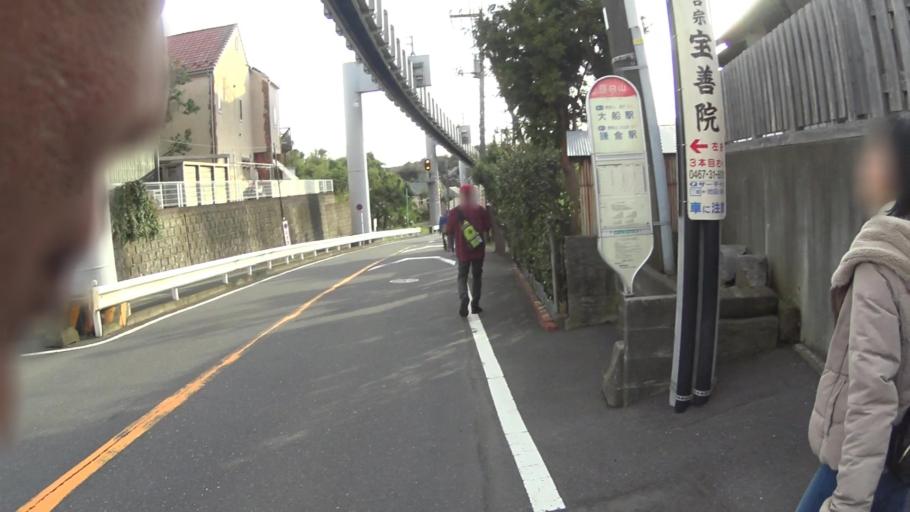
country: JP
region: Kanagawa
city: Fujisawa
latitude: 35.3152
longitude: 139.4934
